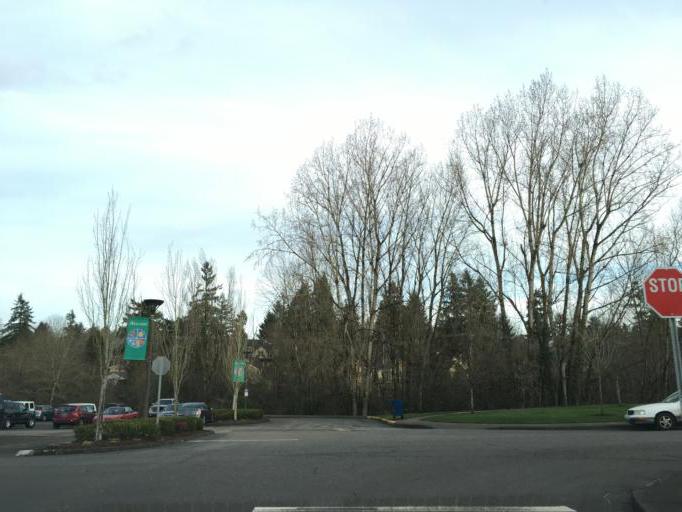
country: US
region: Oregon
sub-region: Clackamas County
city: Lake Oswego
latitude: 45.4330
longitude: -122.7036
